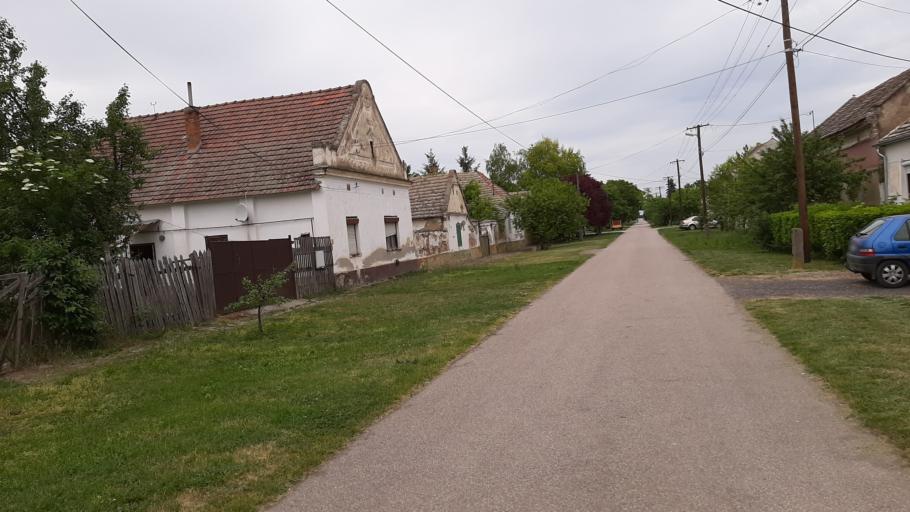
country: RO
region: Timis
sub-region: Comuna Beba Veche
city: Beba Veche
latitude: 46.1463
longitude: 20.2778
